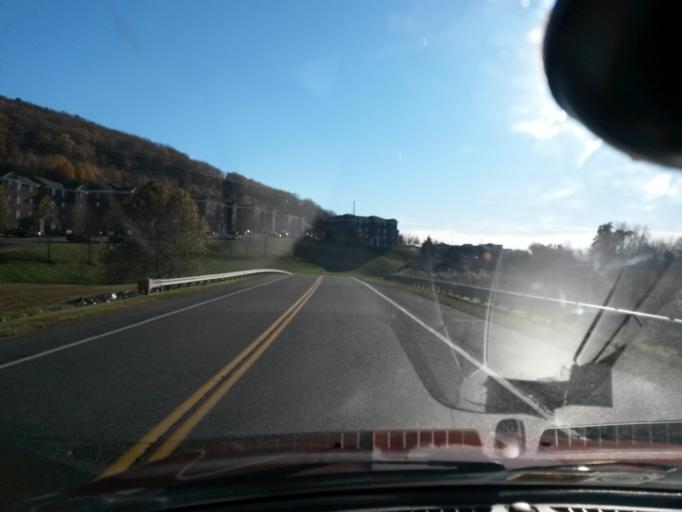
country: US
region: Virginia
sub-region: City of Lynchburg
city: West Lynchburg
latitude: 37.3501
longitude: -79.1756
